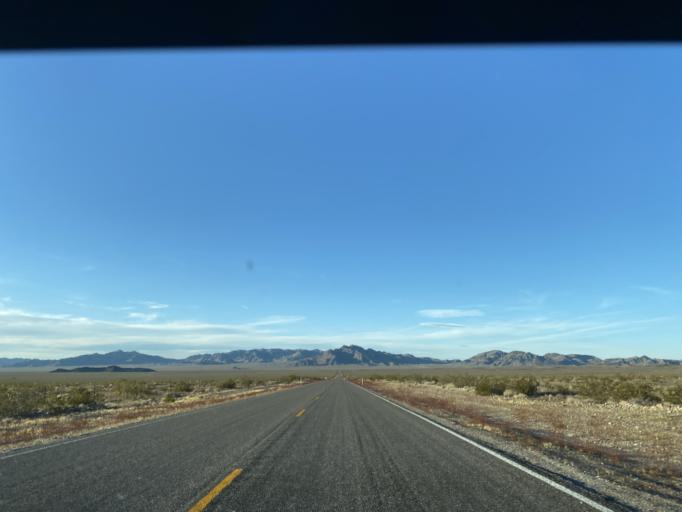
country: US
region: Nevada
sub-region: Nye County
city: Pahrump
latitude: 36.5018
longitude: -116.1171
